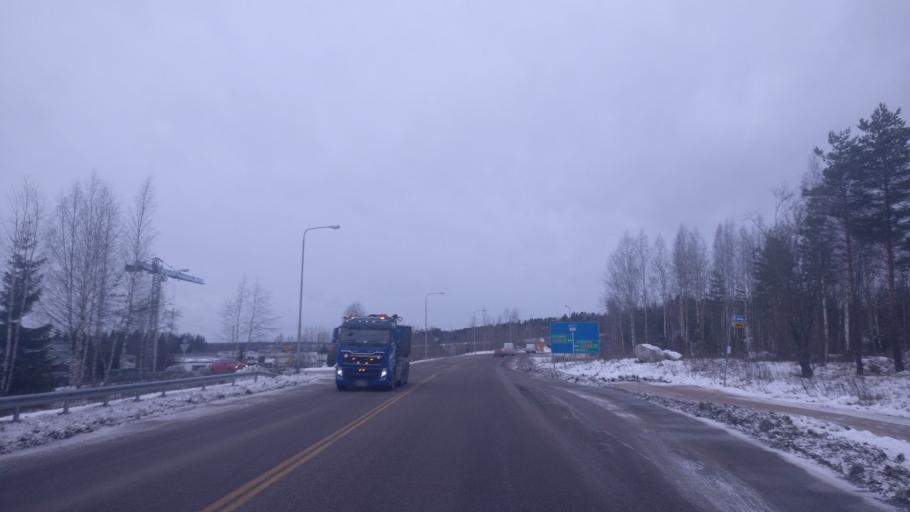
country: FI
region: Paijanne Tavastia
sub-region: Lahti
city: Lahti
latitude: 60.9663
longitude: 25.7218
